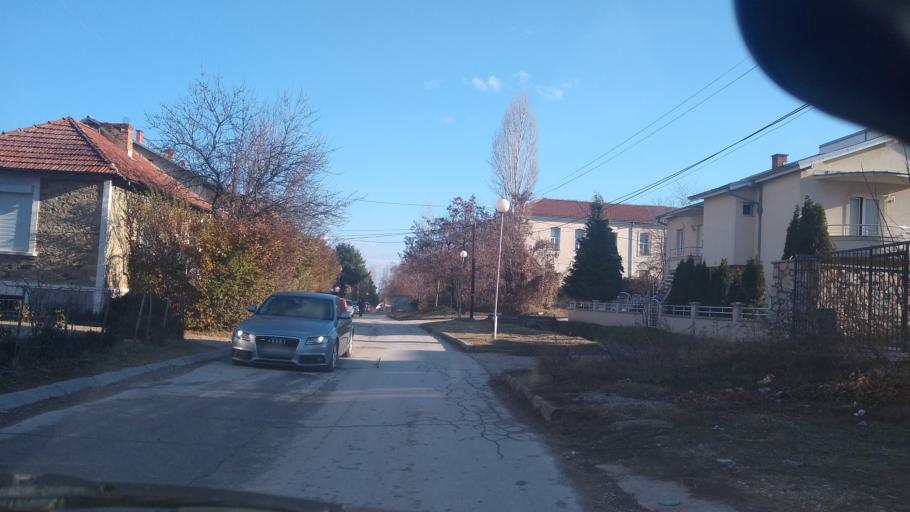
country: MK
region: Bitola
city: Bitola
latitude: 41.0218
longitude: 21.3218
